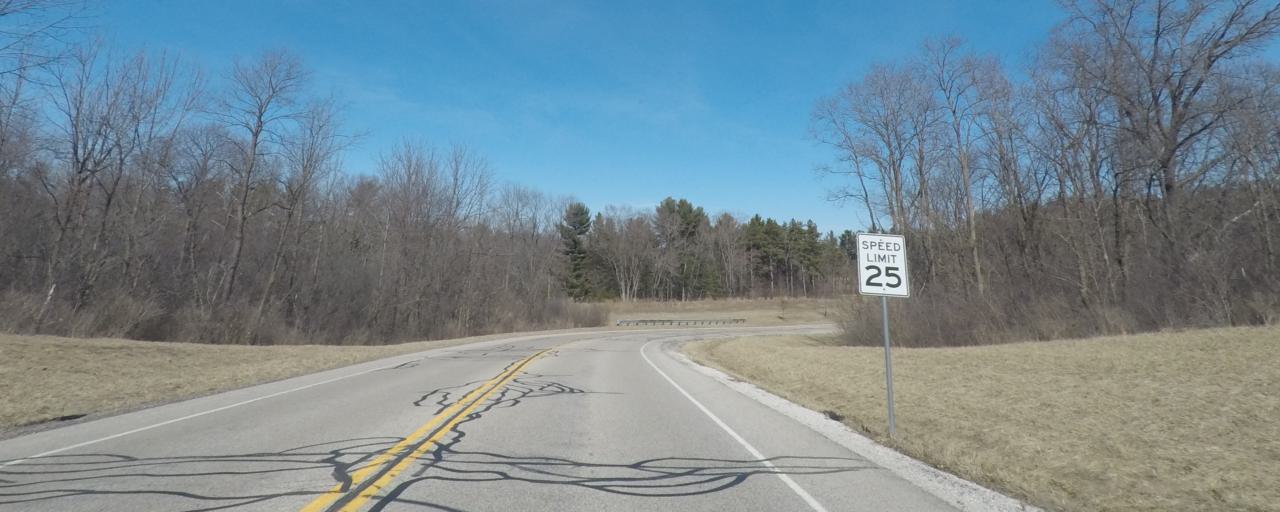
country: US
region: Wisconsin
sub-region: Waukesha County
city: Hartland
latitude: 43.1173
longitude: -88.3545
